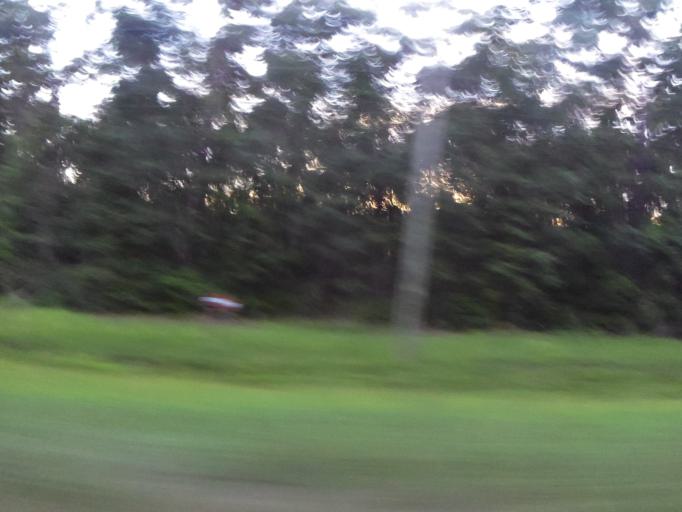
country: US
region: Georgia
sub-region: Camden County
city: Kingsland
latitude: 30.8689
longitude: -81.7041
